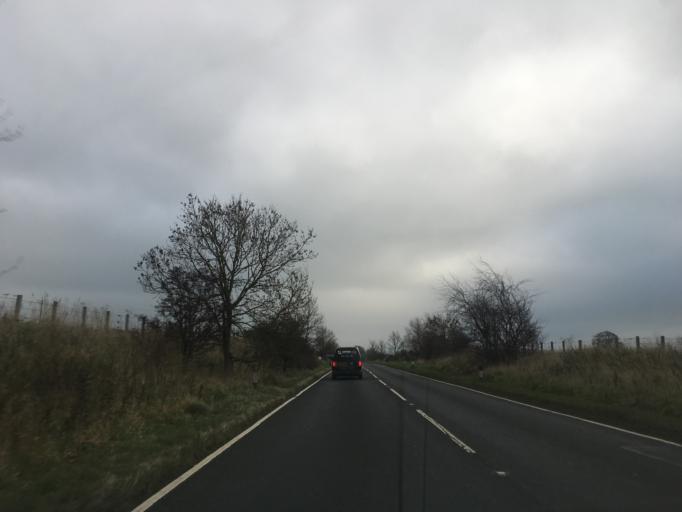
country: GB
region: Scotland
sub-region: Fife
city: Auchtermuchty
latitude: 56.2993
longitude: -3.1891
